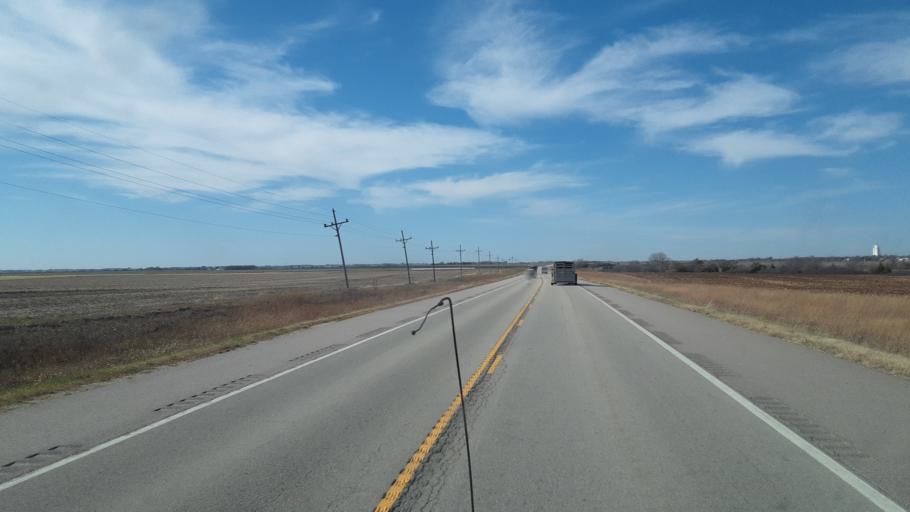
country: US
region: Kansas
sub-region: Marion County
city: Hillsboro
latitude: 38.3624
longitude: -97.2714
